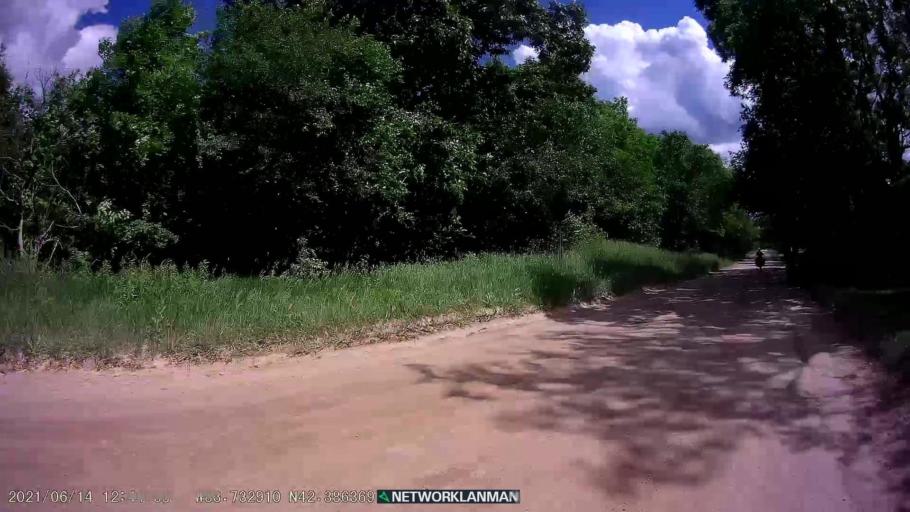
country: US
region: Michigan
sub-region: Livingston County
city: Whitmore Lake
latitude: 42.3861
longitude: -83.7329
